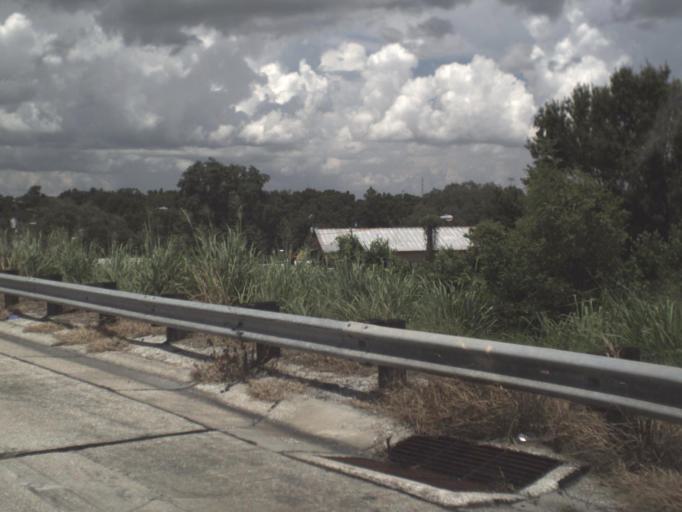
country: US
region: Florida
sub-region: Hillsborough County
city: Temple Terrace
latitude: 28.0369
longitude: -82.3487
